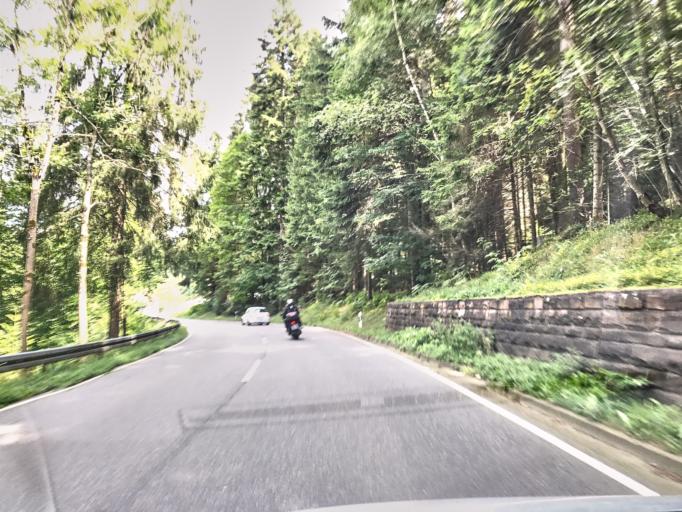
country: DE
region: Baden-Wuerttemberg
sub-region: Karlsruhe Region
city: Lossburg
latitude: 48.3813
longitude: 8.4271
